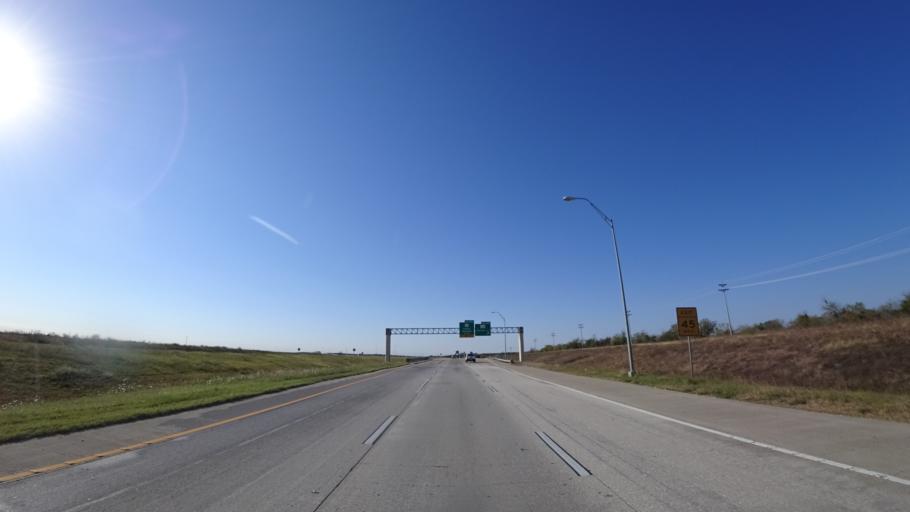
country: US
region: Texas
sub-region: Travis County
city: Manor
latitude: 30.3580
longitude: -97.5889
